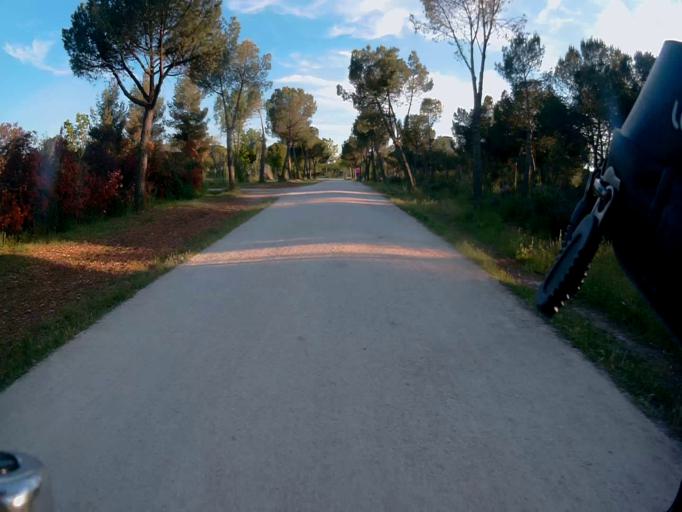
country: ES
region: Madrid
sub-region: Provincia de Madrid
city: Leganes
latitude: 40.3264
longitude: -3.7962
